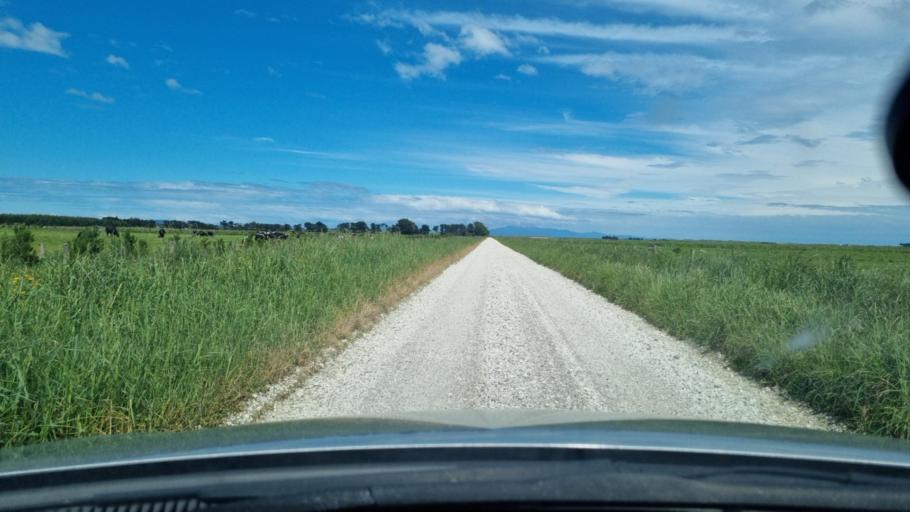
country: NZ
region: Southland
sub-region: Invercargill City
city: Invercargill
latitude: -46.3770
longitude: 168.2730
